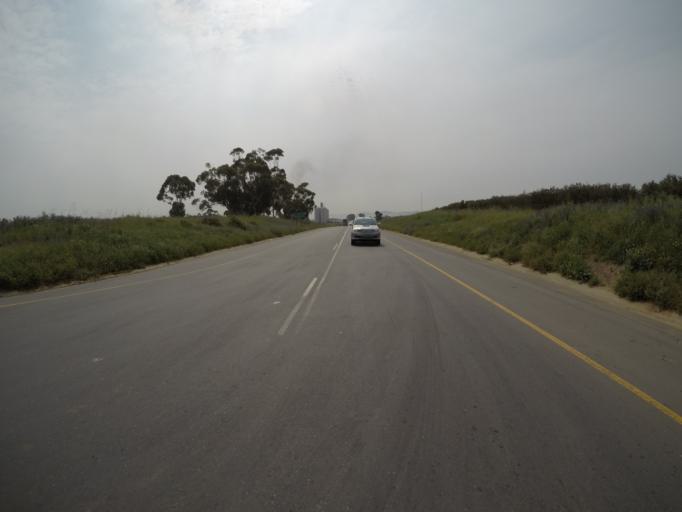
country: ZA
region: Western Cape
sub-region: City of Cape Town
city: Kraaifontein
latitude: -33.7083
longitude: 18.6982
